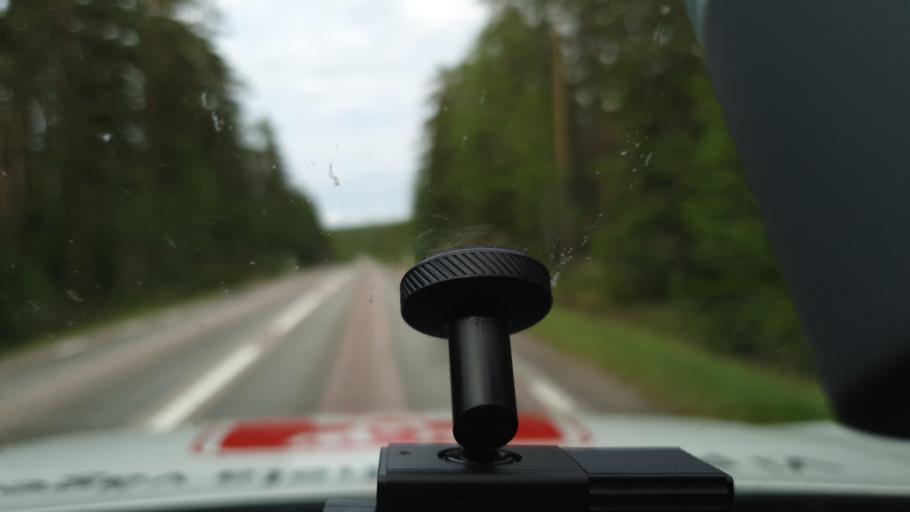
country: SE
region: Vaermland
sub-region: Torsby Kommun
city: Torsby
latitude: 60.3206
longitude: 13.1151
